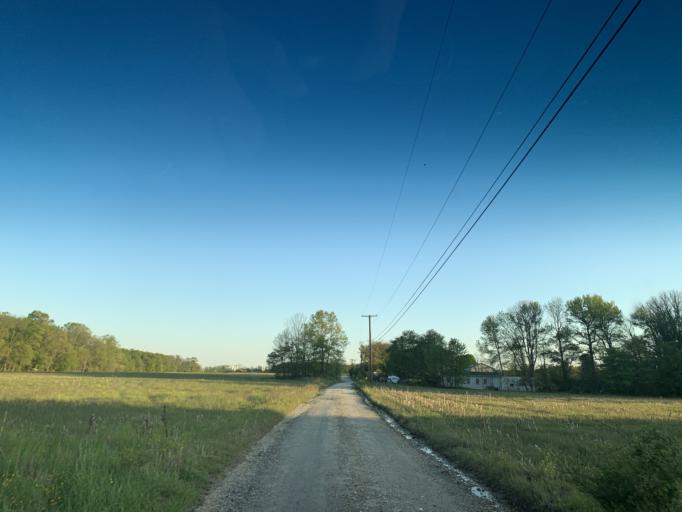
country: US
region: Maryland
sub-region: Harford County
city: Aberdeen
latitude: 39.5099
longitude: -76.1903
